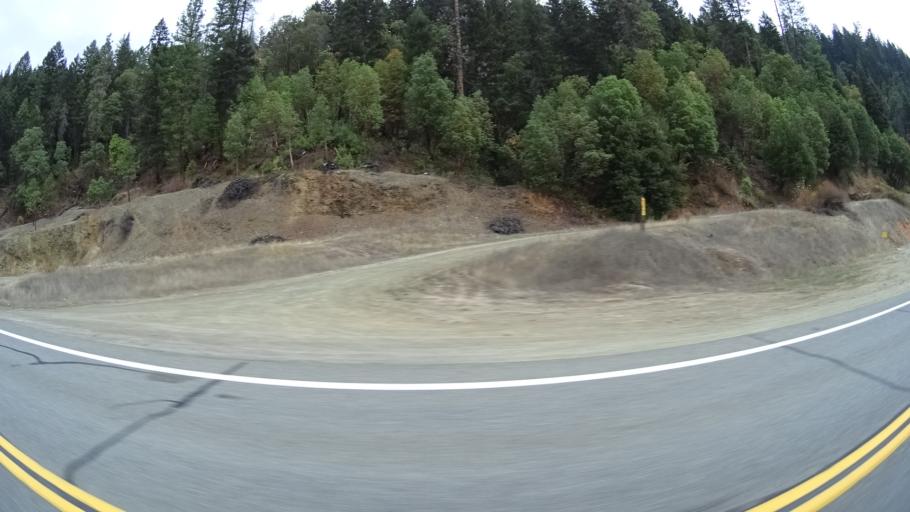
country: US
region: California
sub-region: Siskiyou County
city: Happy Camp
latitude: 41.8110
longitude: -123.3540
